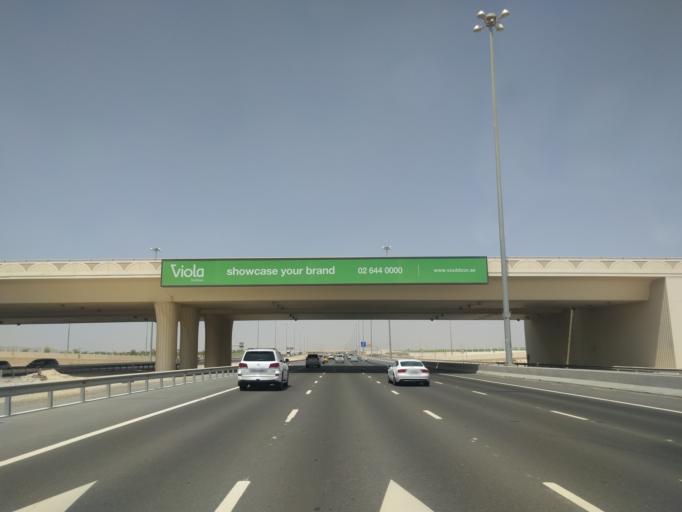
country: AE
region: Abu Dhabi
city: Abu Dhabi
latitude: 24.6854
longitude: 54.7728
